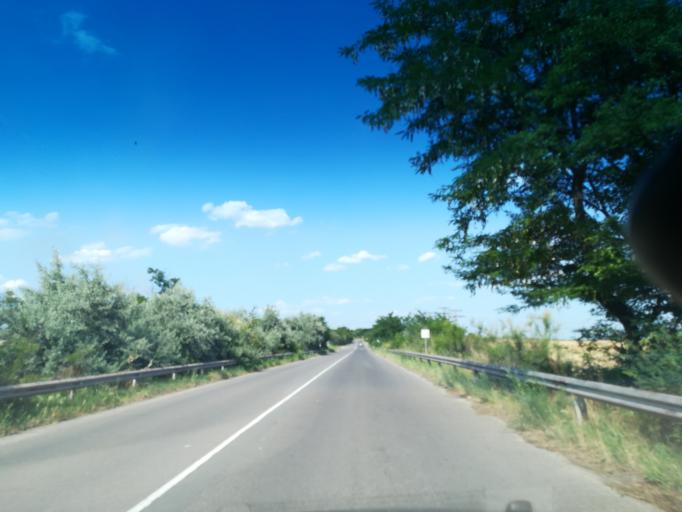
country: BG
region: Stara Zagora
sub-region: Obshtina Chirpan
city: Chirpan
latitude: 42.2066
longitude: 25.3551
